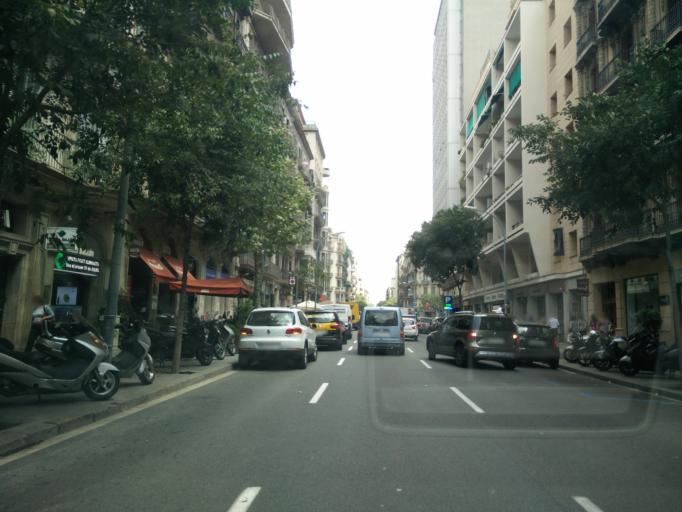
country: ES
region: Catalonia
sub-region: Provincia de Barcelona
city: Barcelona
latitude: 41.3936
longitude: 2.1579
